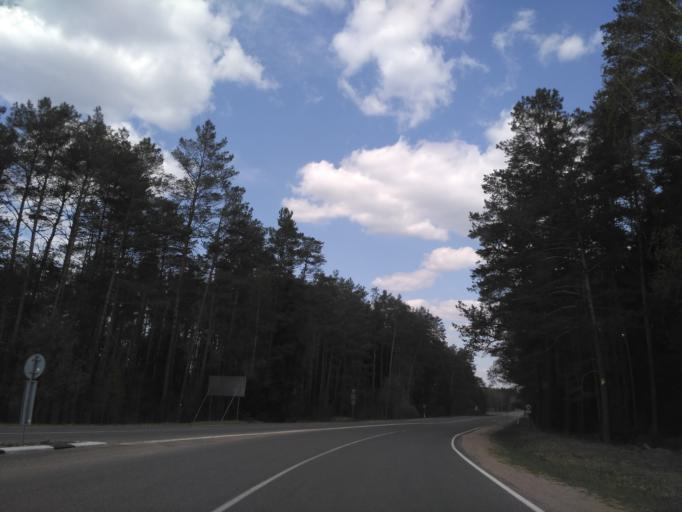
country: BY
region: Minsk
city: Myadzyel
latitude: 54.7722
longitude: 26.9491
